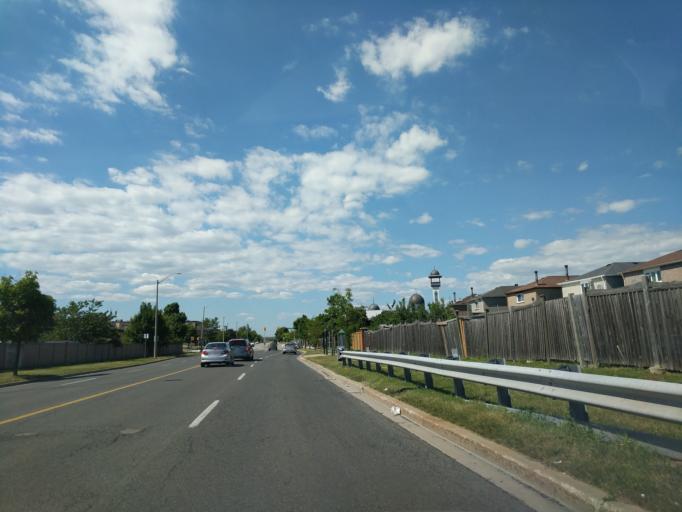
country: CA
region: Ontario
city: Markham
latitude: 43.8402
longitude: -79.2646
